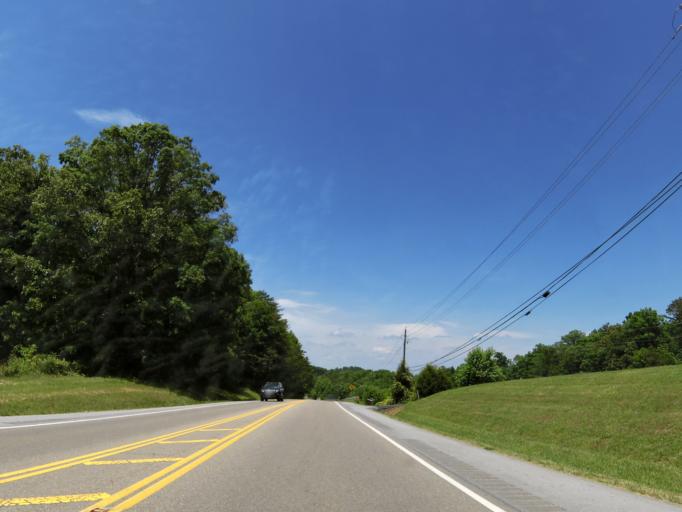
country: US
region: Tennessee
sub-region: Jefferson County
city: Dandridge
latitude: 35.9081
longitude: -83.4031
